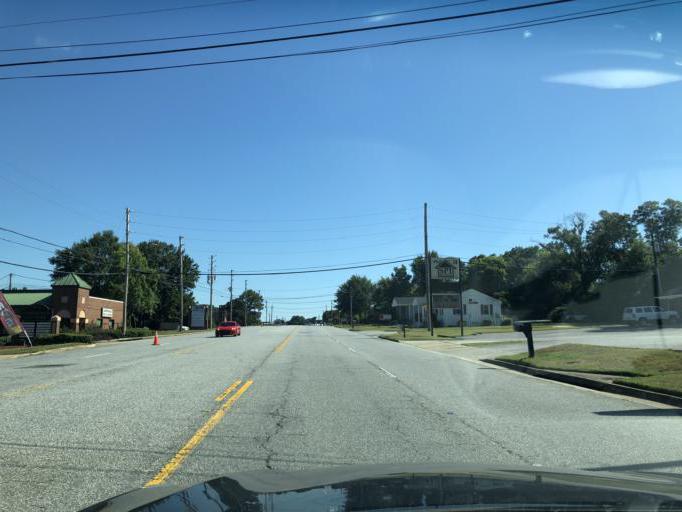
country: US
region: Georgia
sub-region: Muscogee County
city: Columbus
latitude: 32.5117
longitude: -84.9538
